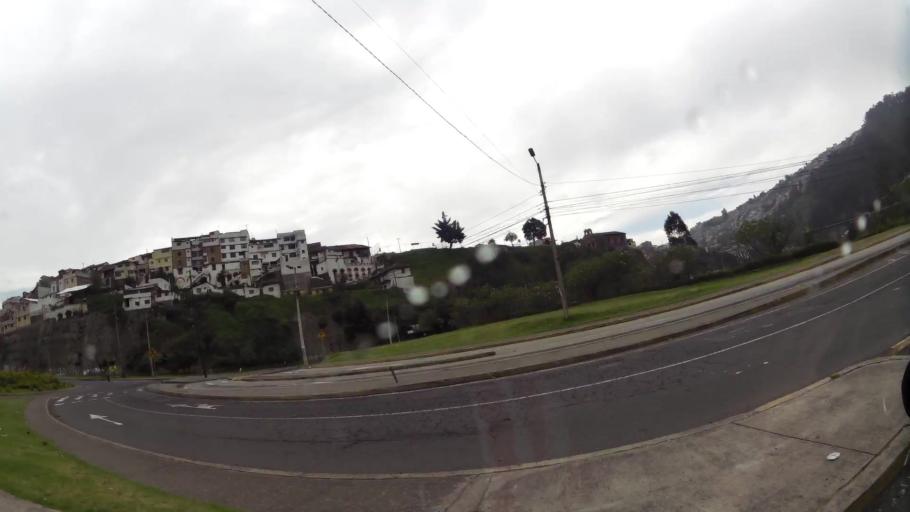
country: EC
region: Pichincha
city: Quito
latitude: -0.2310
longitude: -78.5101
